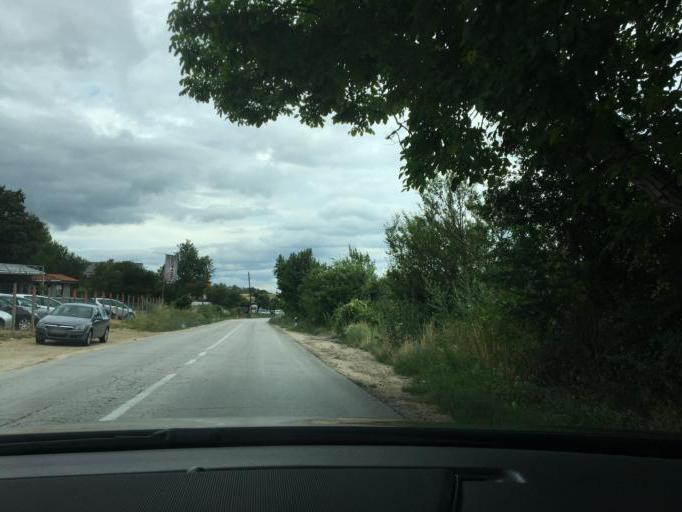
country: MK
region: Kriva Palanka
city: Kriva Palanka
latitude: 42.1788
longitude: 22.2671
